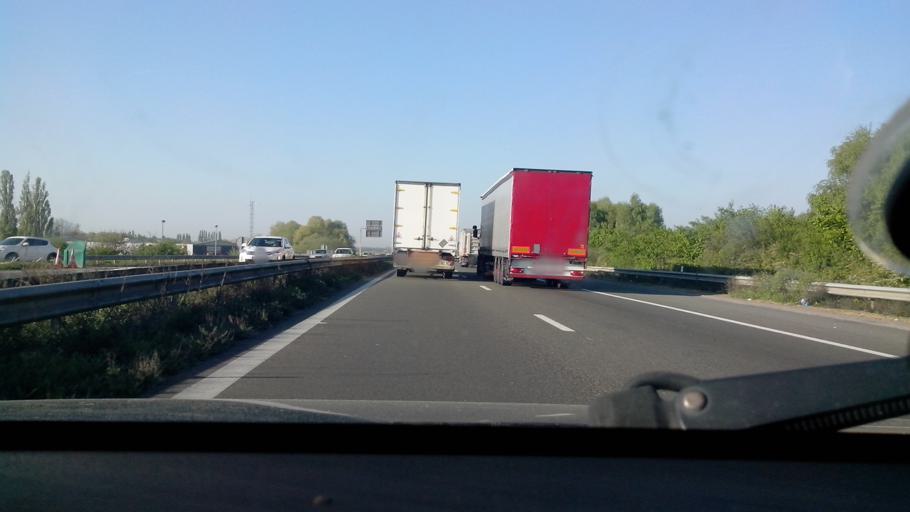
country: FR
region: Ile-de-France
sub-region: Departement de Seine-et-Marne
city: Servon
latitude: 48.7040
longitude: 2.5969
